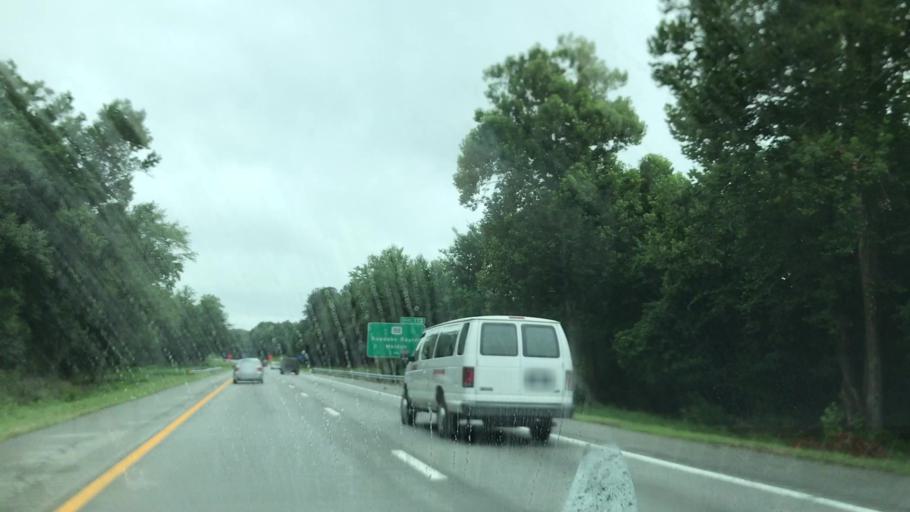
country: US
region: North Carolina
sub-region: Halifax County
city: Weldon
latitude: 36.4123
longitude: -77.6374
